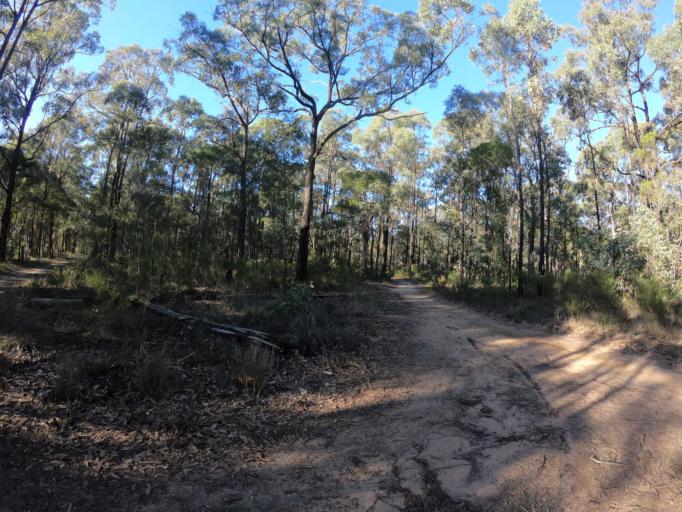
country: AU
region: New South Wales
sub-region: Hawkesbury
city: South Windsor
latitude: -33.6421
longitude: 150.7961
